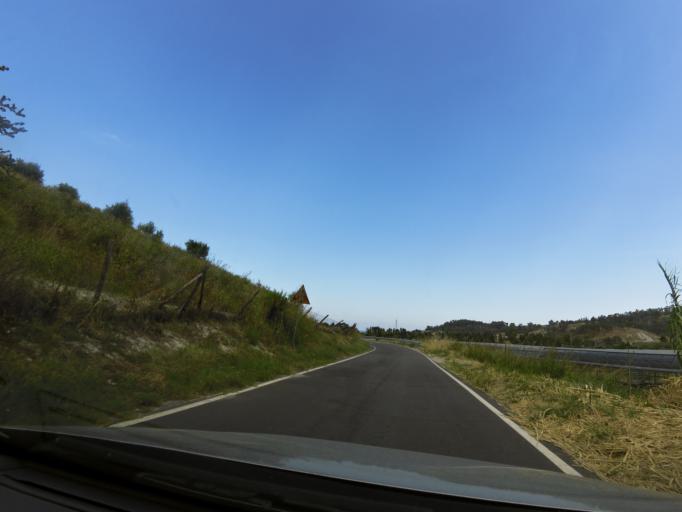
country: IT
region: Calabria
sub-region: Provincia di Reggio Calabria
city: Camini
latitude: 38.4292
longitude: 16.5193
